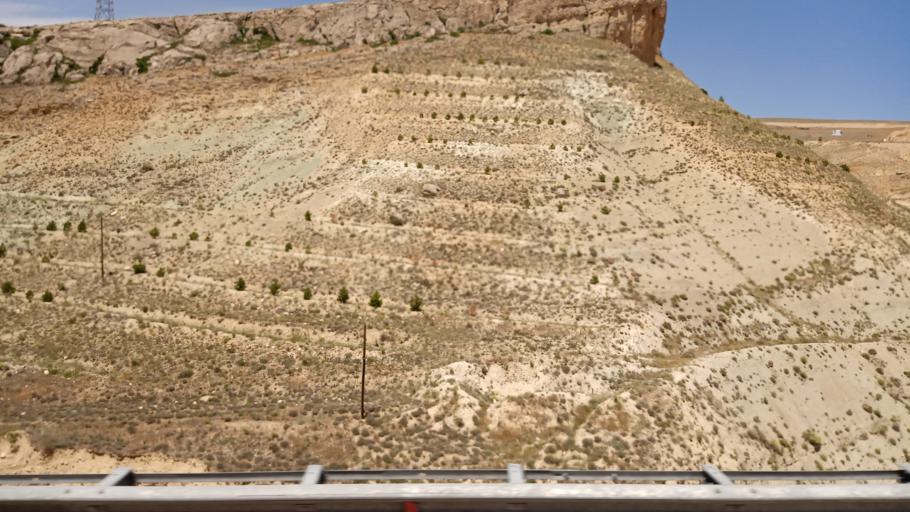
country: TR
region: Malatya
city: Darende
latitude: 38.5762
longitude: 37.4643
